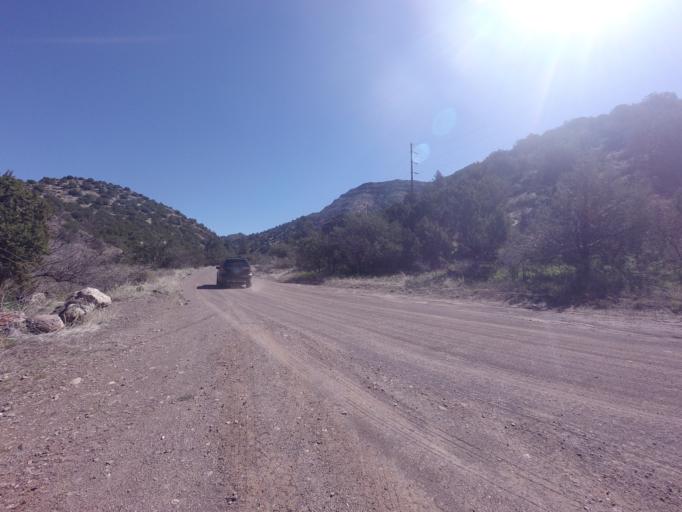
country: US
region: Arizona
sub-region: Gila County
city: Pine
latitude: 34.4000
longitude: -111.6237
